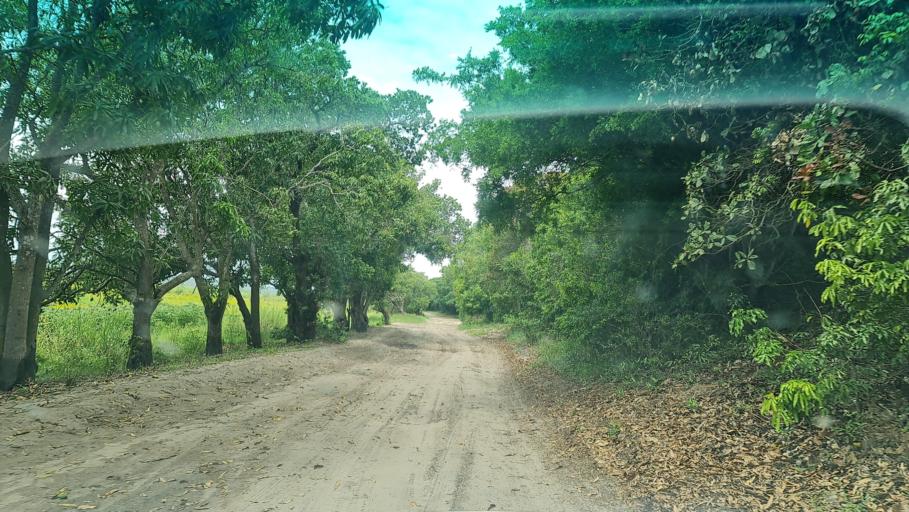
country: MZ
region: Maputo
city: Manhica
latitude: -25.5307
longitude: 32.8450
